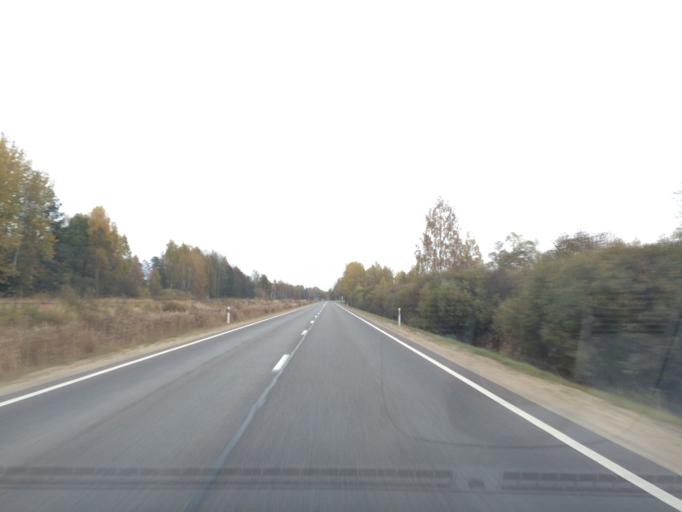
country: LV
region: Livani
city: Livani
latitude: 56.5461
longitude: 26.1084
